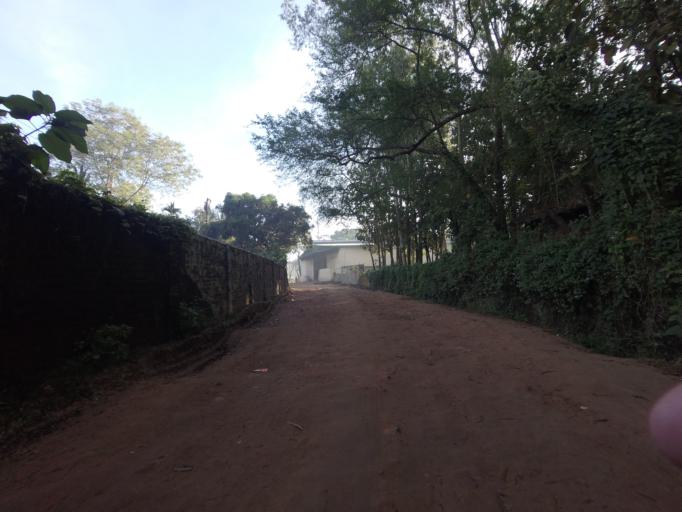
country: BD
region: Chittagong
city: Fatikchari
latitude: 22.5819
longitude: 91.6839
